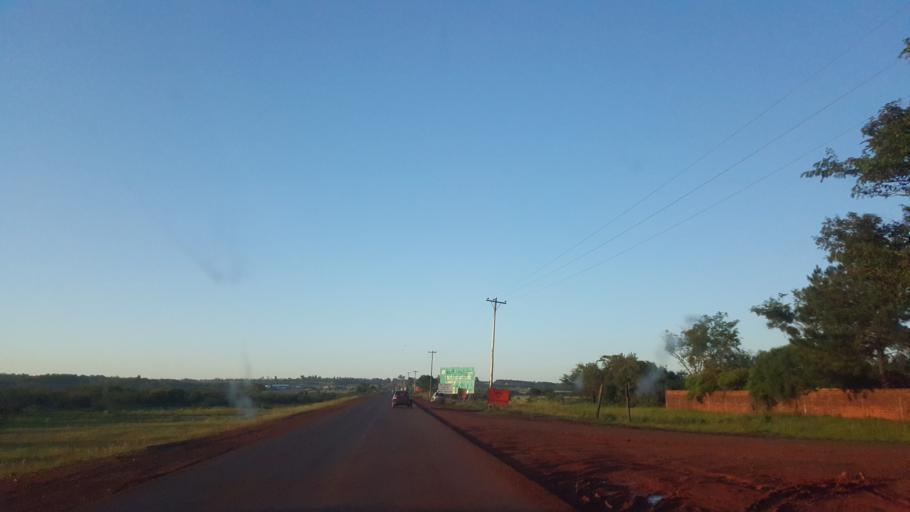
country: AR
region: Corrientes
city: Santo Tome
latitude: -28.5434
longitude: -56.0492
